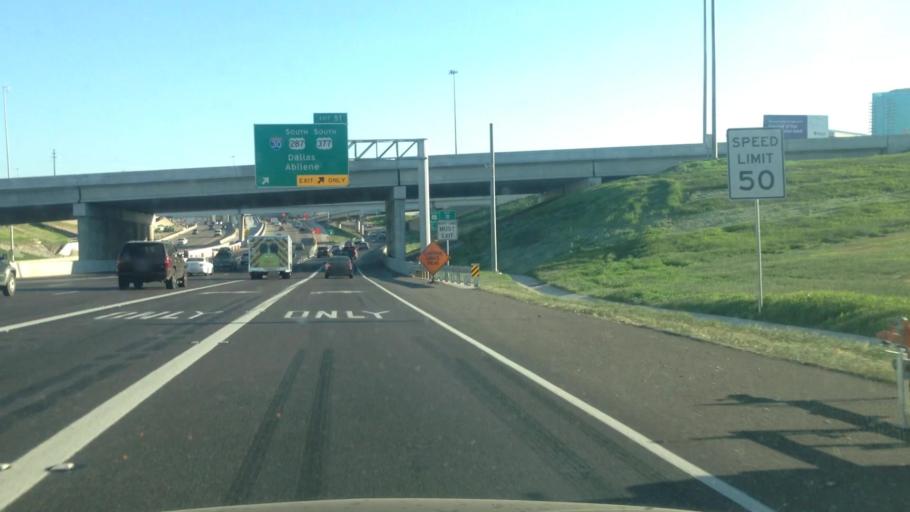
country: US
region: Texas
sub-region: Tarrant County
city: Fort Worth
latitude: 32.7571
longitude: -97.3193
